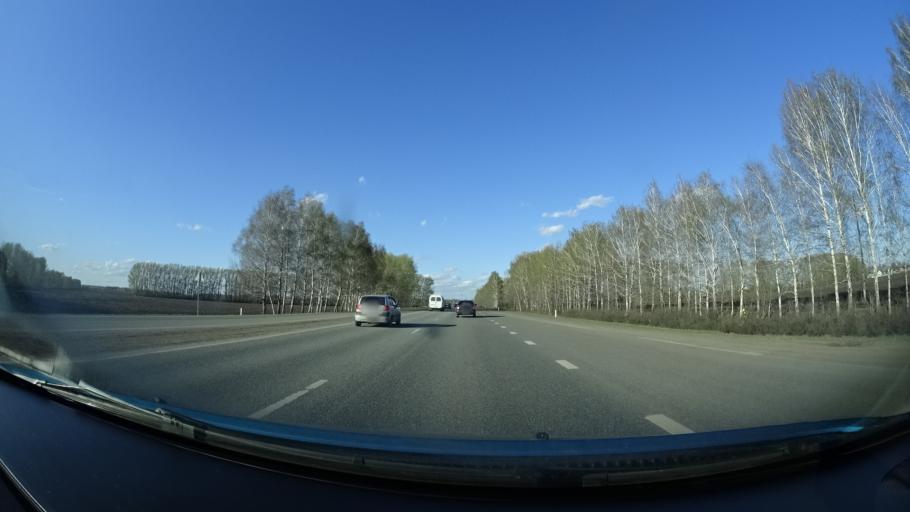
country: RU
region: Bashkortostan
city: Ufa
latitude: 54.5480
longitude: 55.9195
